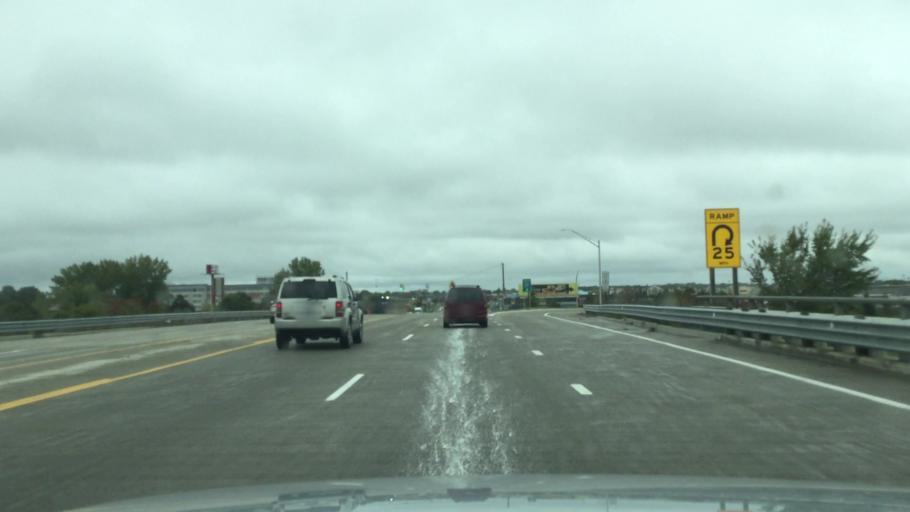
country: US
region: Michigan
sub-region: Saginaw County
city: Carrollton
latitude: 43.4799
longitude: -83.9563
